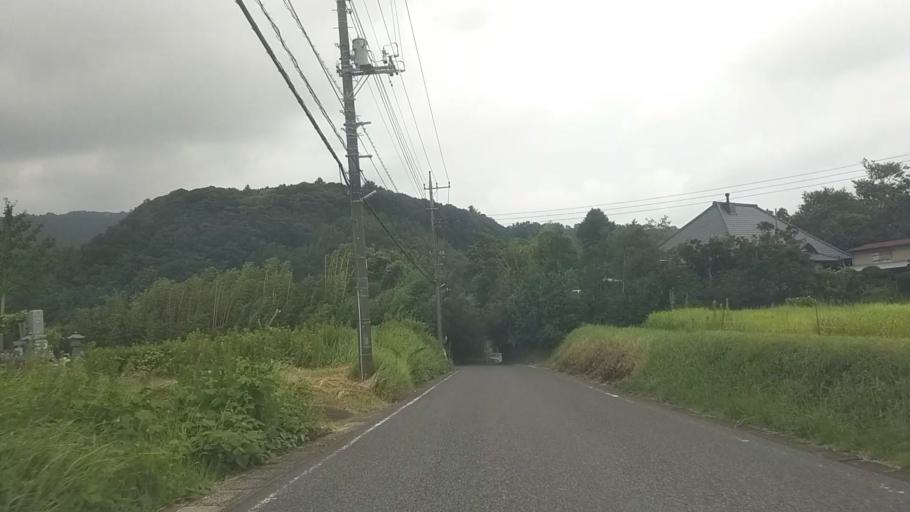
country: JP
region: Chiba
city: Kimitsu
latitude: 35.2470
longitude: 139.9925
